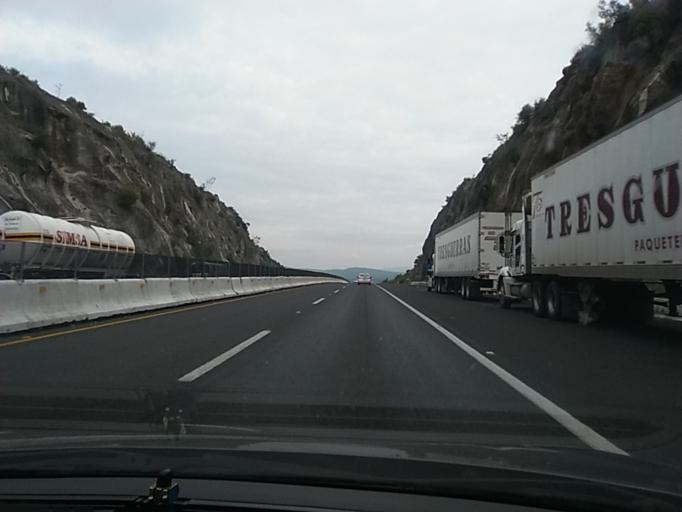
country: MX
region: Michoacan
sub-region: Puruandiro
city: San Lorenzo
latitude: 19.9416
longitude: -101.6281
